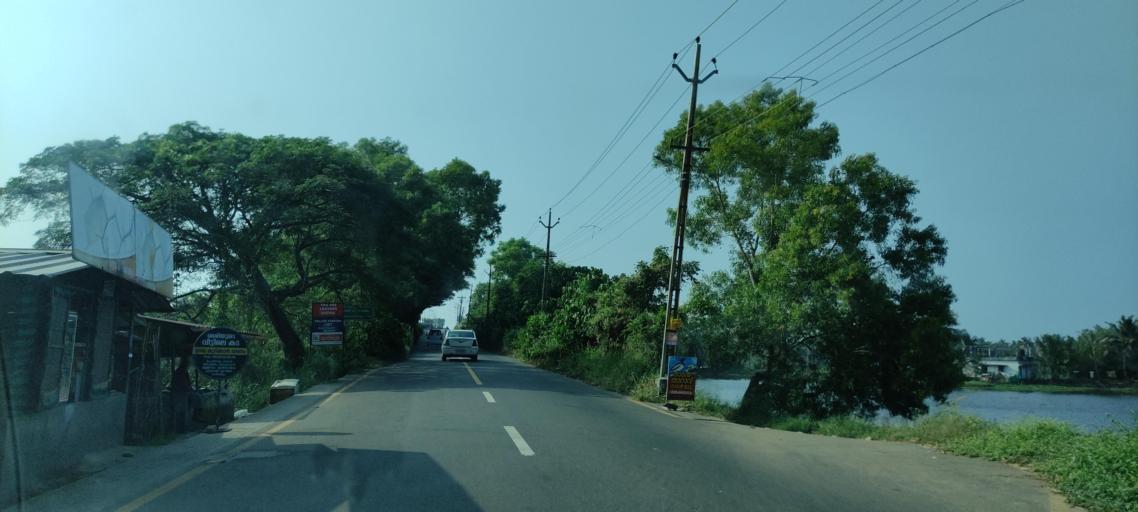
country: IN
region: Kerala
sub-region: Kottayam
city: Changanacheri
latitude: 9.3694
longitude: 76.4270
